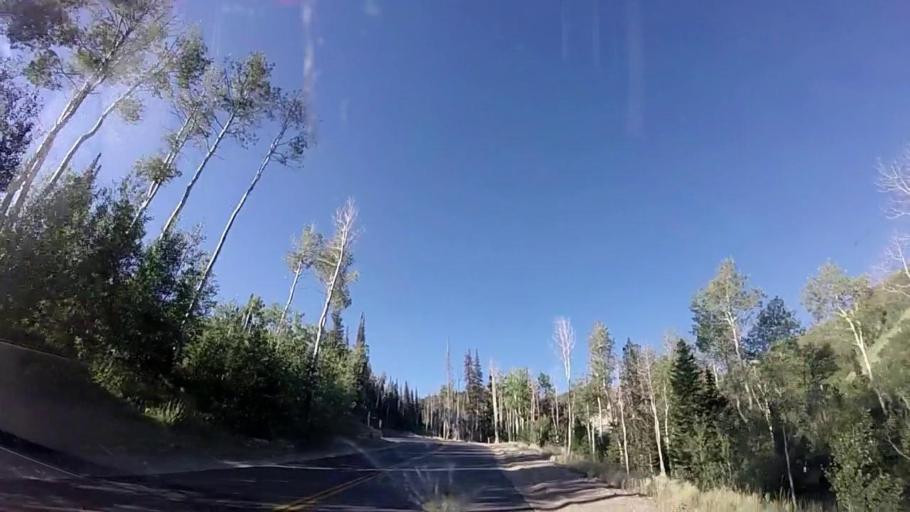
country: US
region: Utah
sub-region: Summit County
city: Park City
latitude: 40.6195
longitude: -111.5075
